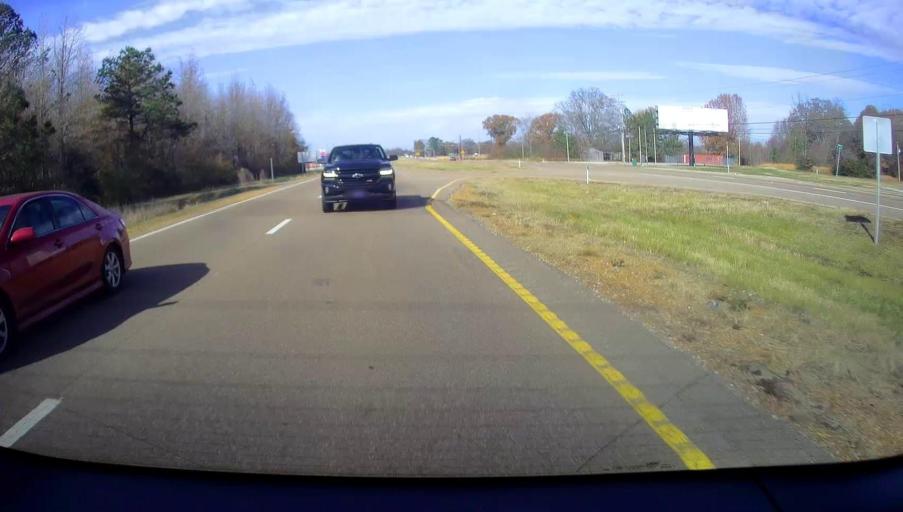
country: US
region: Tennessee
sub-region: Fayette County
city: Piperton
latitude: 34.9928
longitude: -89.6151
